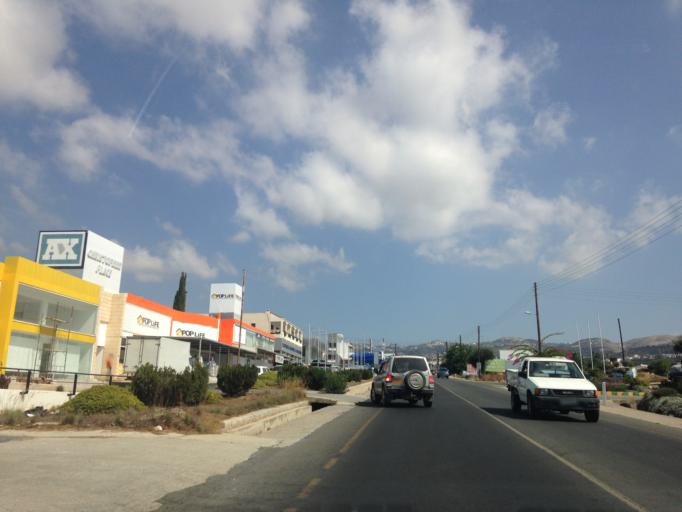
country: CY
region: Pafos
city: Empa
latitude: 34.8008
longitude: 32.4425
